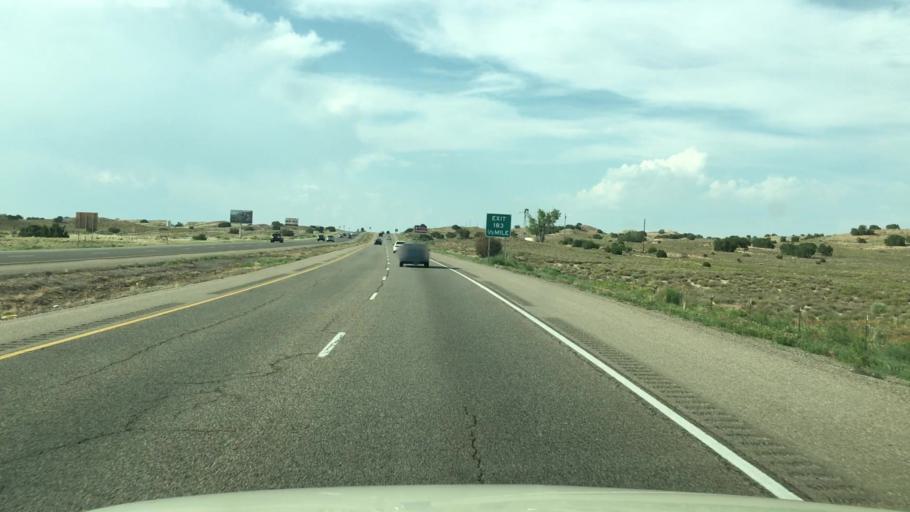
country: US
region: New Mexico
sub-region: Santa Fe County
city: Pojoaque
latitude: 35.9164
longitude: -106.0164
